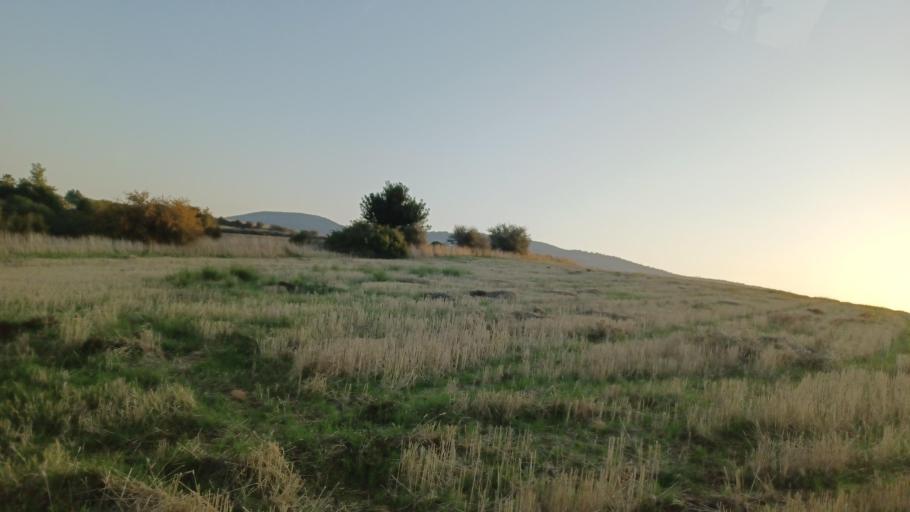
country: CY
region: Pafos
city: Polis
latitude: 35.0007
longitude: 32.4496
